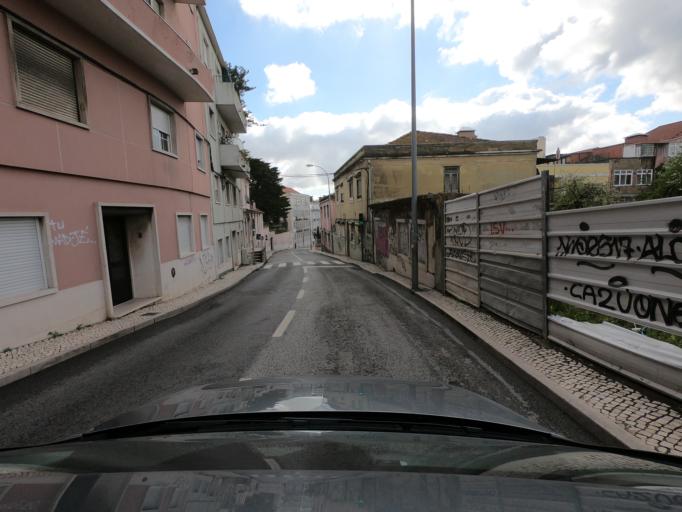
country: PT
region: Lisbon
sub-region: Oeiras
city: Alges
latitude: 38.7006
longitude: -9.2348
